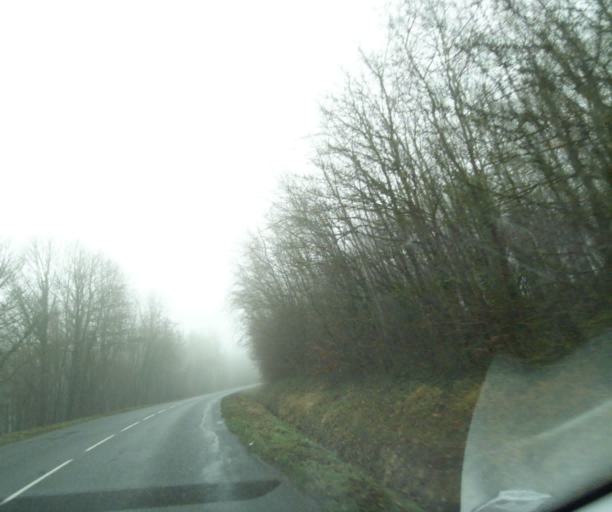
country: FR
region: Ile-de-France
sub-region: Departement de Seine-et-Marne
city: Saint-Mard
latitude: 49.0452
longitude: 2.6883
